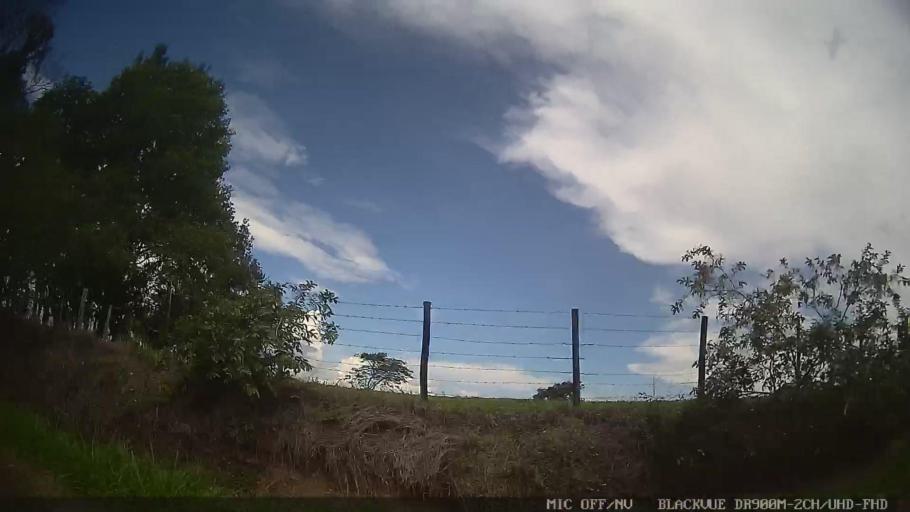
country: BR
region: Sao Paulo
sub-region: Conchas
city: Conchas
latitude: -22.9623
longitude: -47.9816
